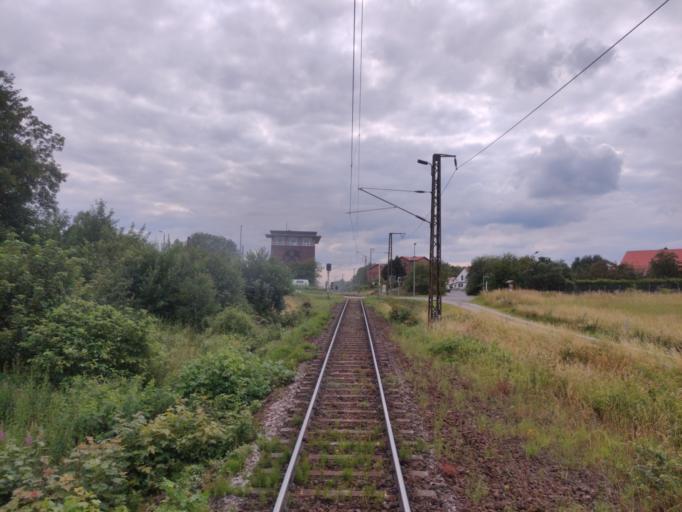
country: DE
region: Saxony-Anhalt
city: Huttenrode
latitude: 51.7720
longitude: 10.9011
